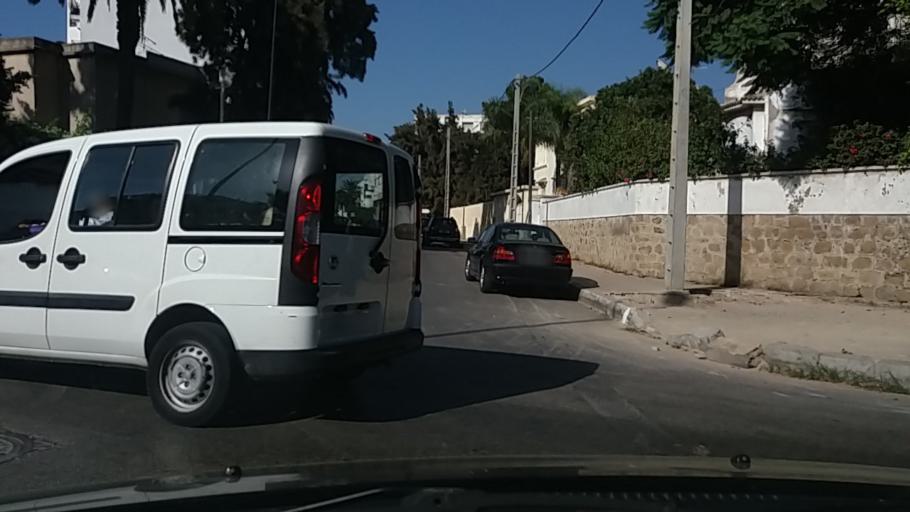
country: MA
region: Rabat-Sale-Zemmour-Zaer
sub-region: Rabat
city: Rabat
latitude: 34.0164
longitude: -6.8276
